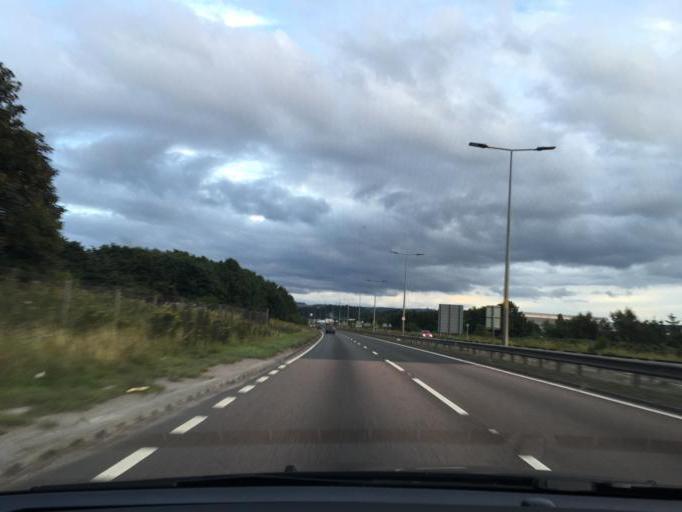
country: GB
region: Scotland
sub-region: Highland
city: Inverness
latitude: 57.4902
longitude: -4.2123
